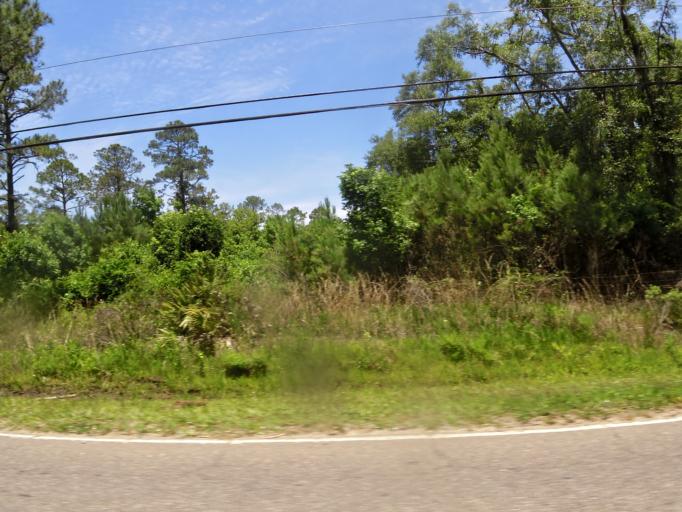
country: US
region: Florida
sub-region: Duval County
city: Jacksonville
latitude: 30.4640
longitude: -81.5468
